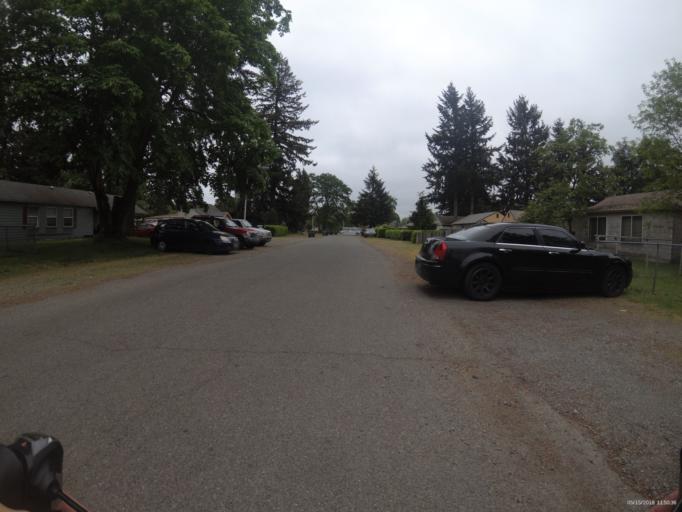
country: US
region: Washington
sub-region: Pierce County
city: Lakewood
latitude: 47.1743
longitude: -122.5214
